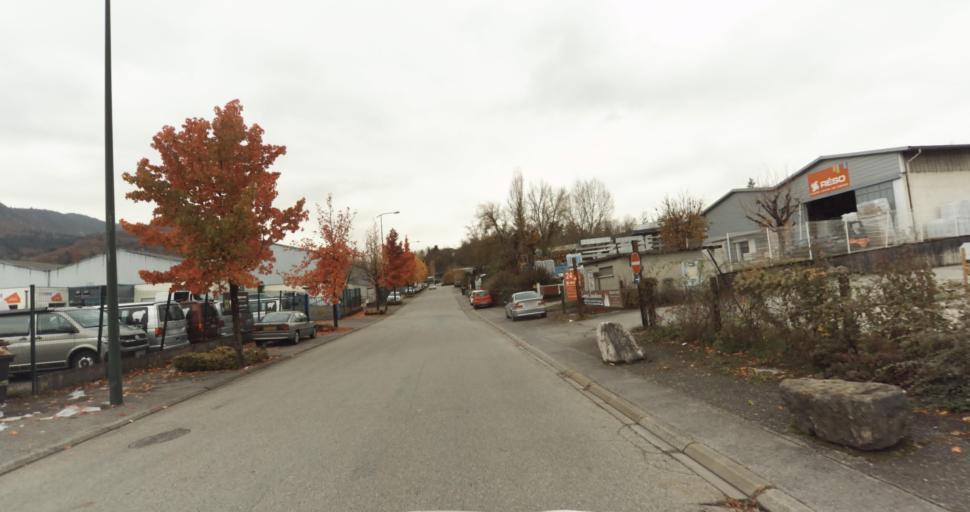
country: FR
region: Rhone-Alpes
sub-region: Departement de la Haute-Savoie
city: Annecy
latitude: 45.8860
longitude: 6.1133
